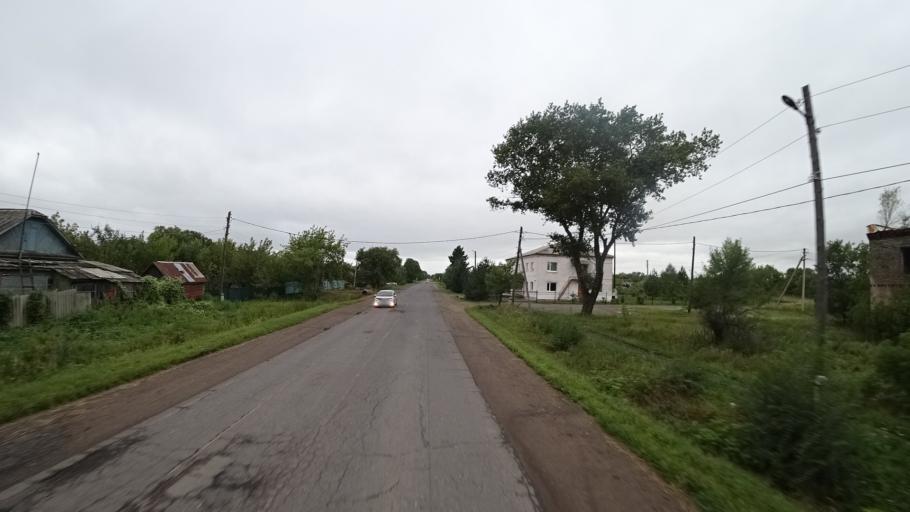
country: RU
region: Primorskiy
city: Chernigovka
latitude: 44.3475
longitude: 132.5598
